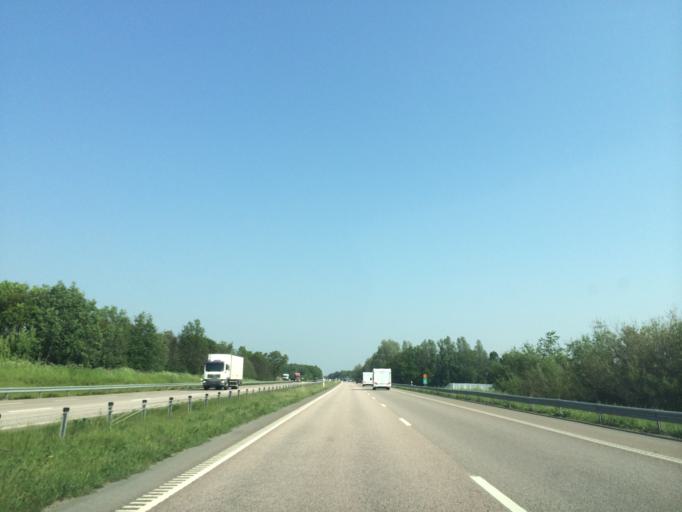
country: SE
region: Skane
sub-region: Helsingborg
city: Barslov
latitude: 56.0448
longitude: 12.7858
